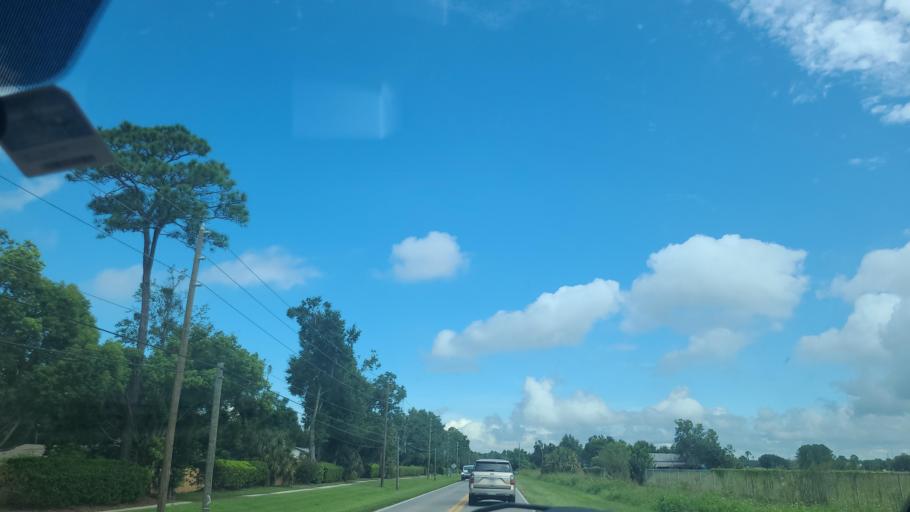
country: US
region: Florida
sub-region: Orange County
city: Ocoee
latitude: 28.5885
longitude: -81.5511
